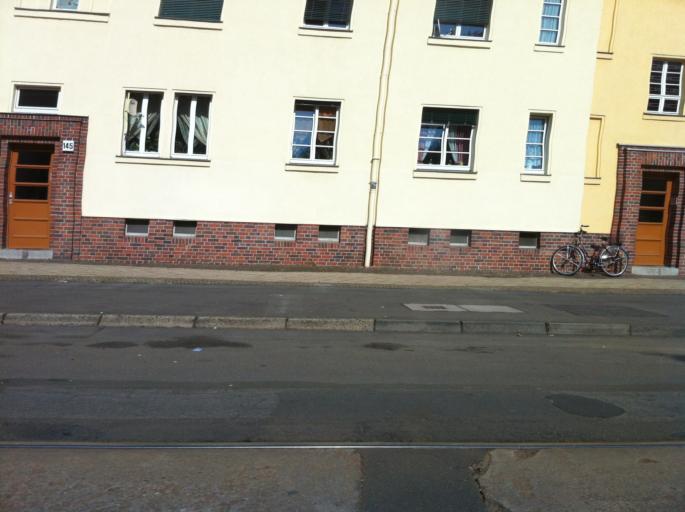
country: DE
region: Saxony
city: Markkleeberg
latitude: 51.2926
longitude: 12.3888
